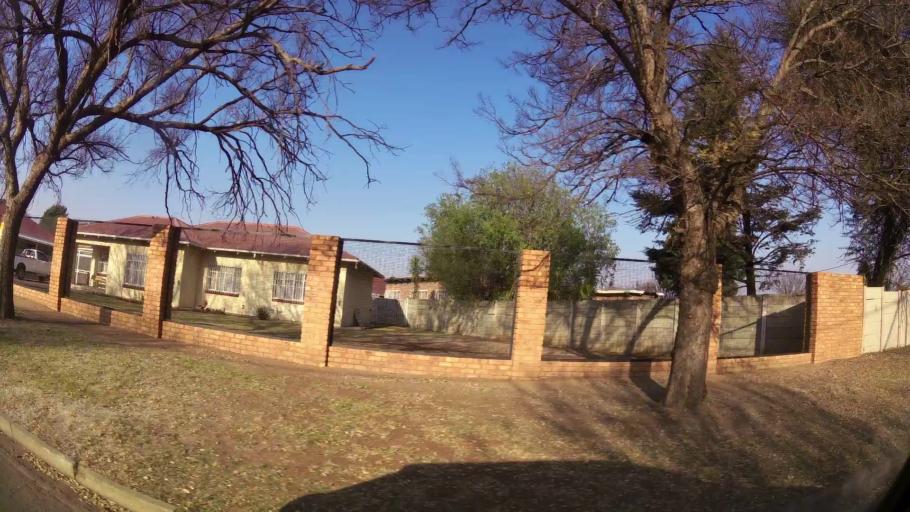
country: ZA
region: Gauteng
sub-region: Ekurhuleni Metropolitan Municipality
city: Springs
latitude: -26.2581
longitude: 28.3870
